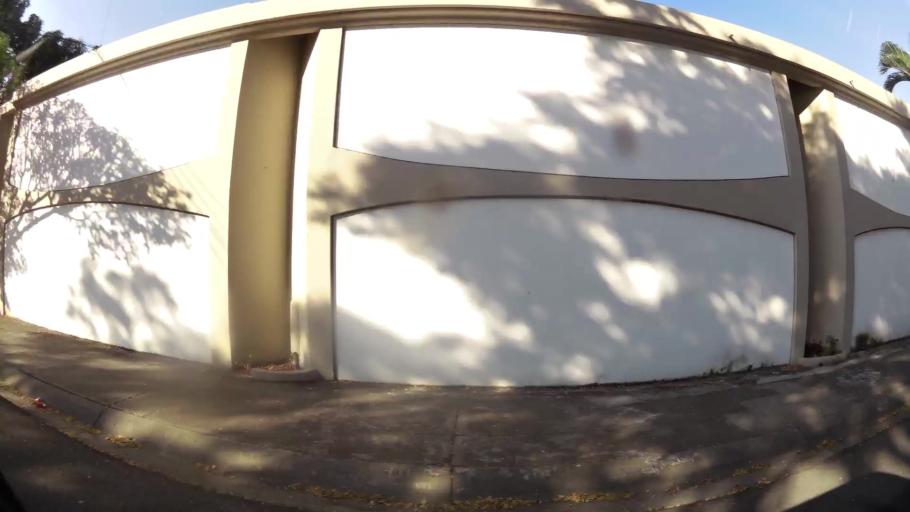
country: EC
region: Guayas
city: Santa Lucia
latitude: -2.1915
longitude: -79.9675
